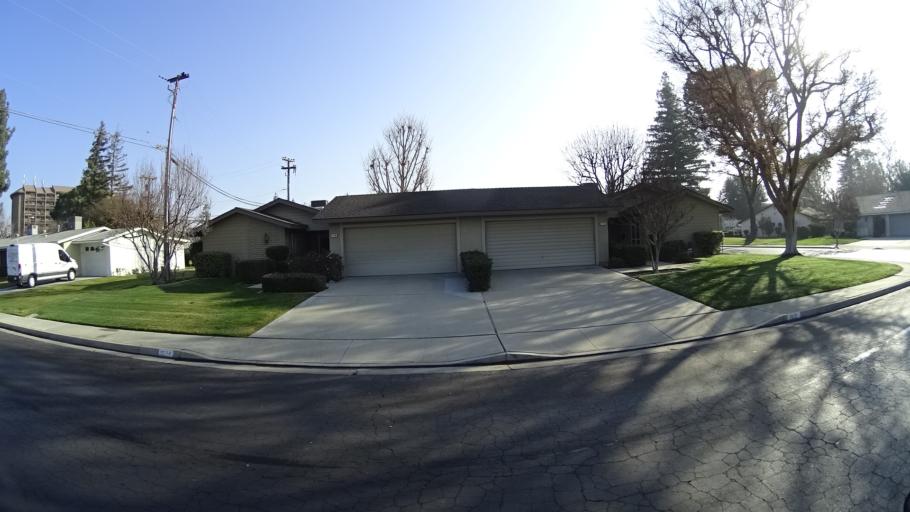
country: US
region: California
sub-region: Kern County
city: Bakersfield
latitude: 35.3414
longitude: -119.0632
